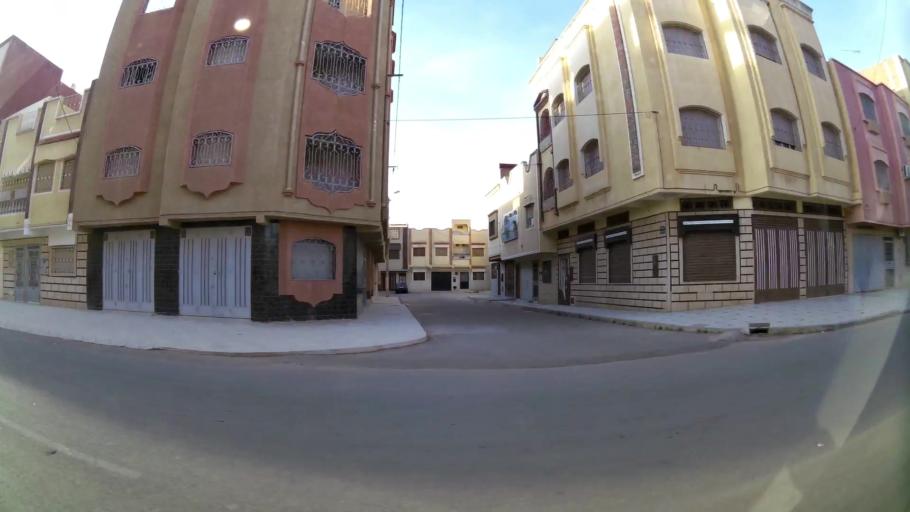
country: MA
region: Oriental
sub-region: Oujda-Angad
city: Oujda
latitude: 34.6773
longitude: -1.8969
